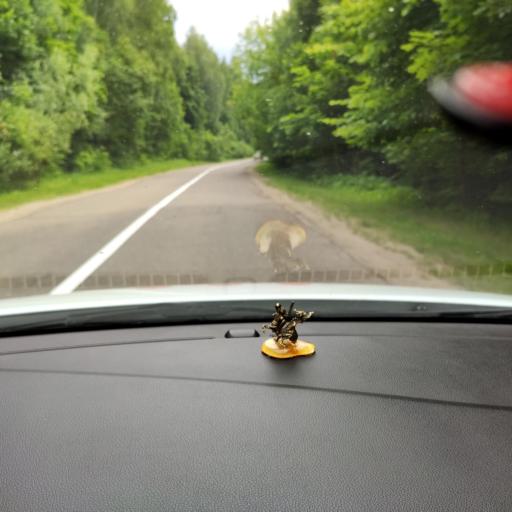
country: RU
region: Tatarstan
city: Kuybyshevskiy Zaton
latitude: 55.3154
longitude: 49.3191
